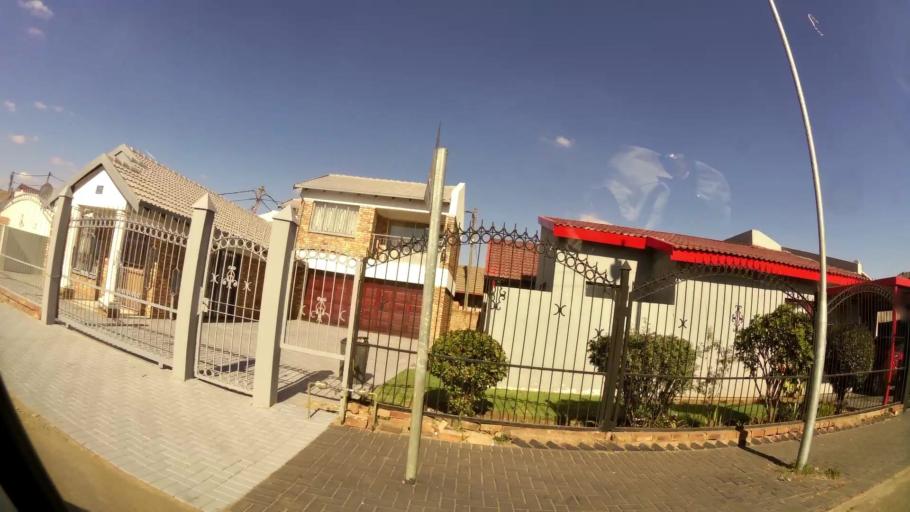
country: ZA
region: Gauteng
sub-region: City of Tshwane Metropolitan Municipality
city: Cullinan
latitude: -25.7147
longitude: 28.3956
